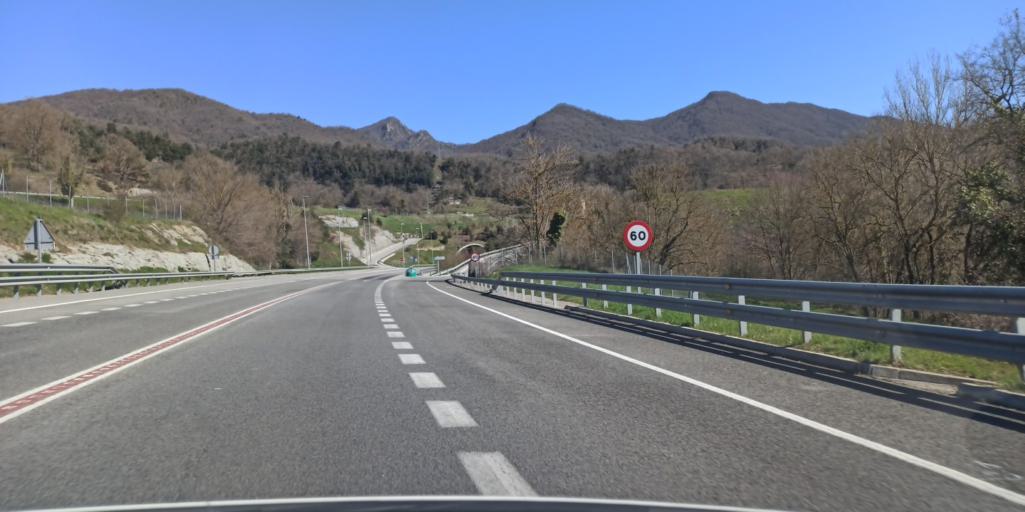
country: ES
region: Catalonia
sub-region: Provincia de Barcelona
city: Santa Maria de Corco
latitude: 42.0878
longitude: 2.3579
